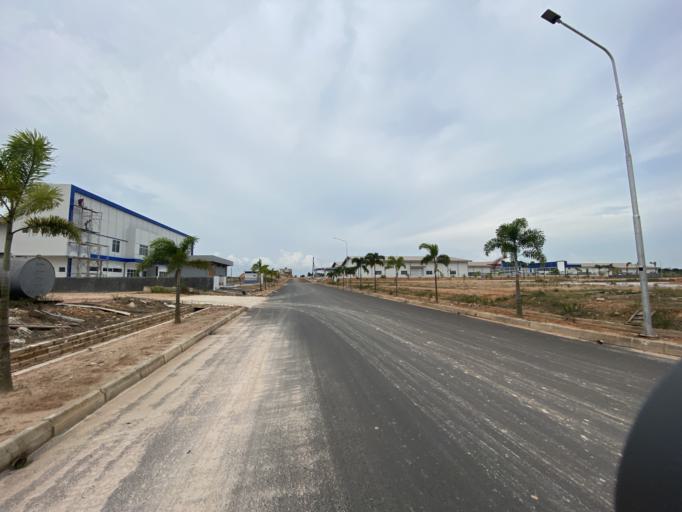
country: SG
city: Singapore
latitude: 1.0214
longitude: 103.9501
